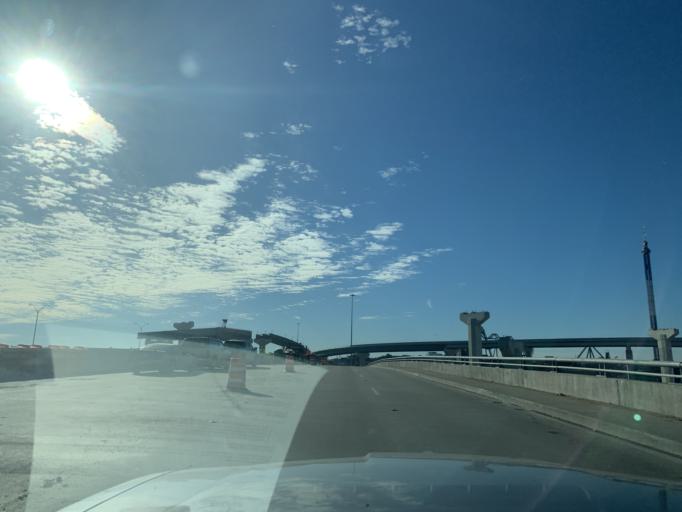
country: US
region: Texas
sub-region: Tarrant County
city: Arlington
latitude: 32.7605
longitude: -97.0643
